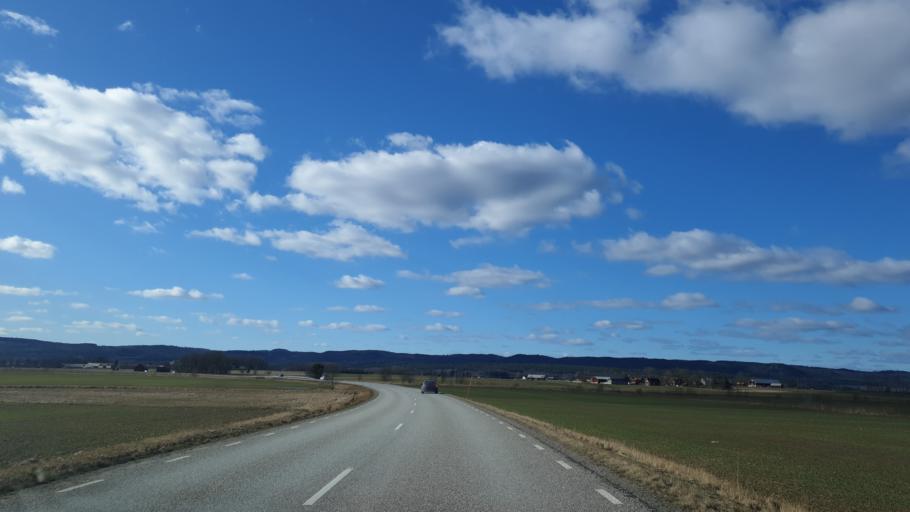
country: SE
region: OErebro
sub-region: Orebro Kommun
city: Garphyttan
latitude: 59.3398
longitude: 15.0590
